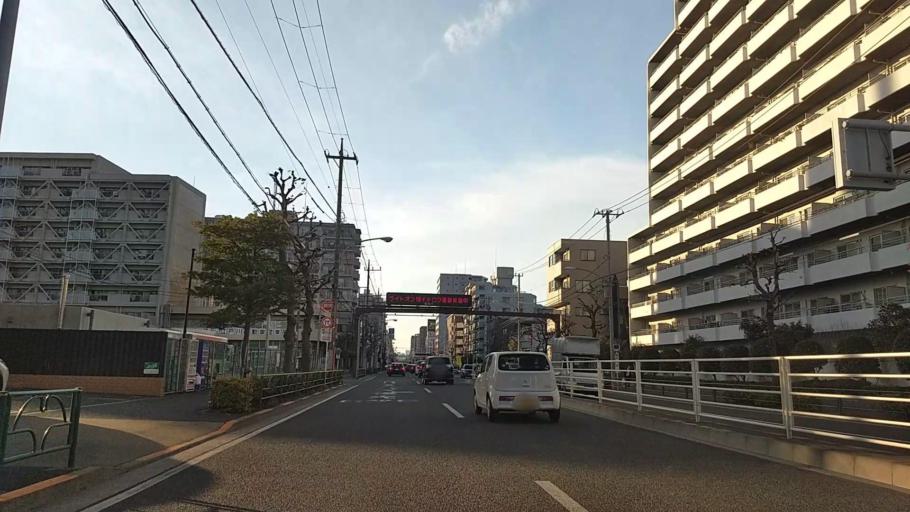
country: JP
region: Tokyo
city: Urayasu
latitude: 35.6684
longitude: 139.8685
